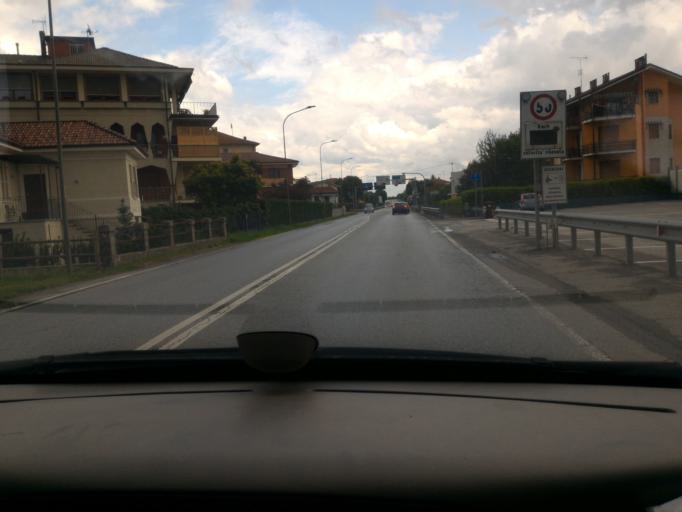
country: IT
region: Piedmont
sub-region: Provincia di Cuneo
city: Savigliano
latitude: 44.6403
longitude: 7.6542
